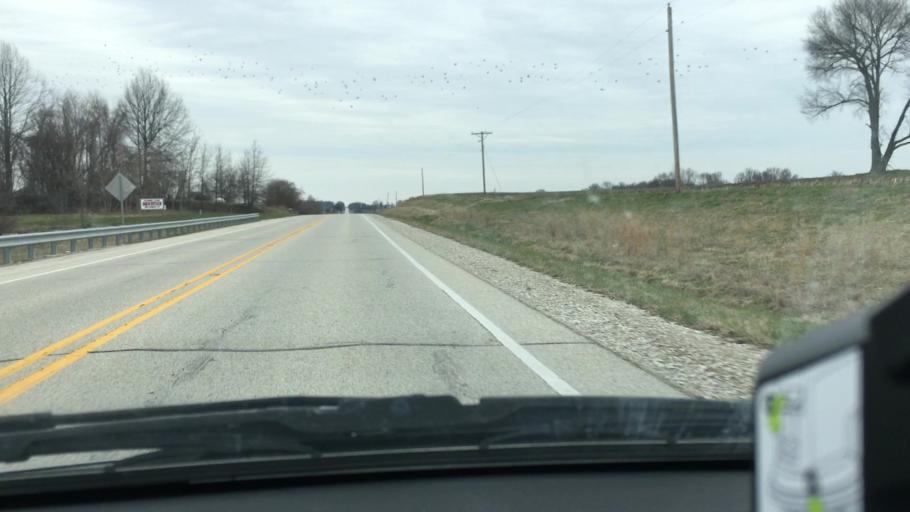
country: US
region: Indiana
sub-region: Greene County
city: Bloomfield
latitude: 38.9636
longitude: -87.0157
